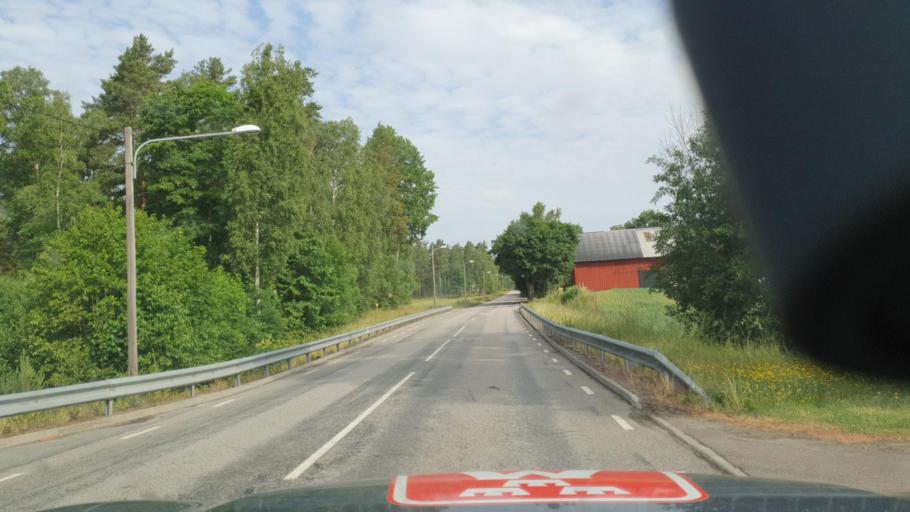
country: SE
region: Kalmar
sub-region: Nybro Kommun
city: Nybro
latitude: 56.6968
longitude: 15.9798
